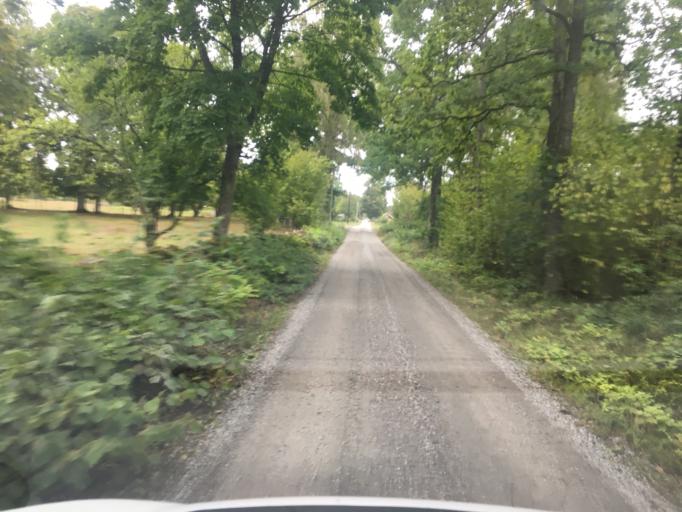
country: SE
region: Kronoberg
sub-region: Ljungby Kommun
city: Lagan
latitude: 56.9723
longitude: 14.0399
